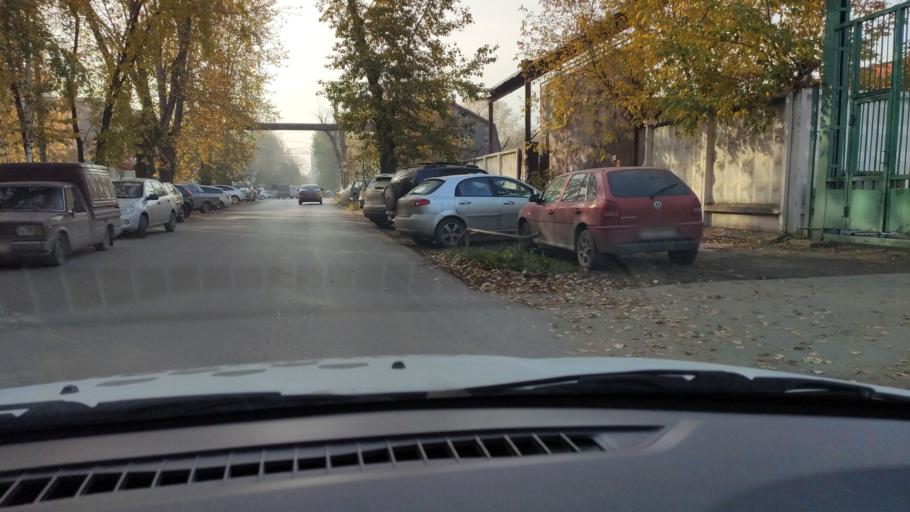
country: RU
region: Perm
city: Perm
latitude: 58.0099
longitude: 56.1826
